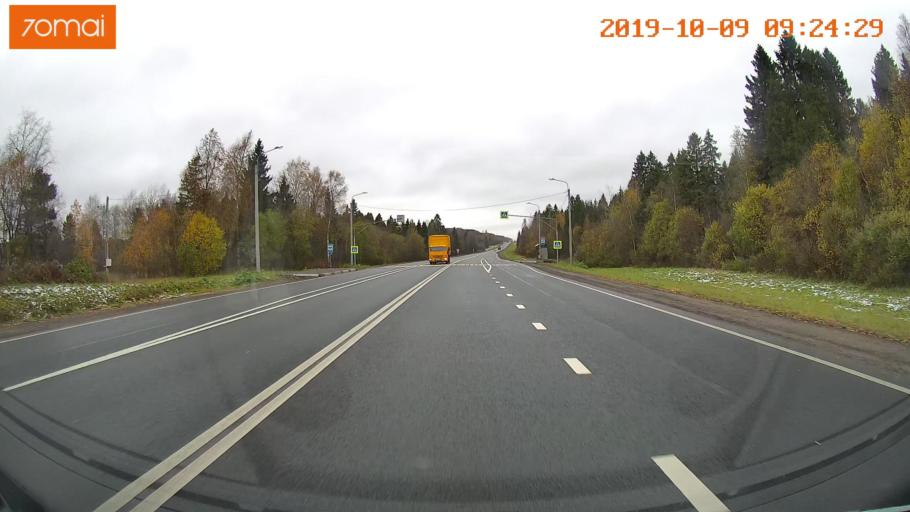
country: RU
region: Vologda
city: Vologda
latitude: 59.0793
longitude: 40.0156
